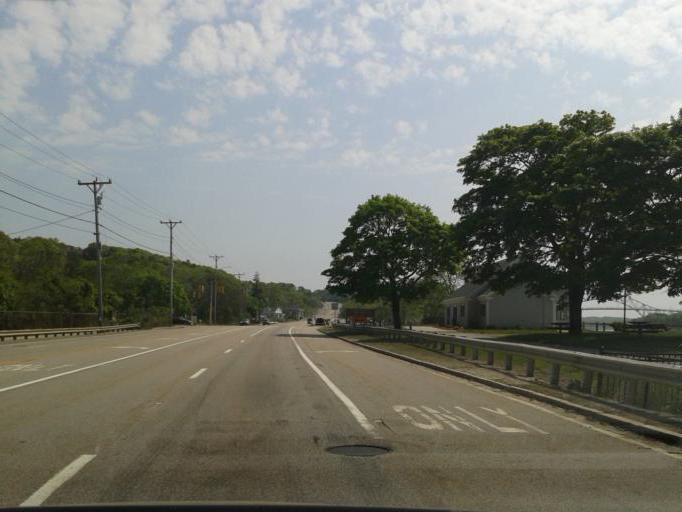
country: US
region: Massachusetts
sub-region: Barnstable County
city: Sagamore
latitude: 41.7726
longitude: -70.5625
